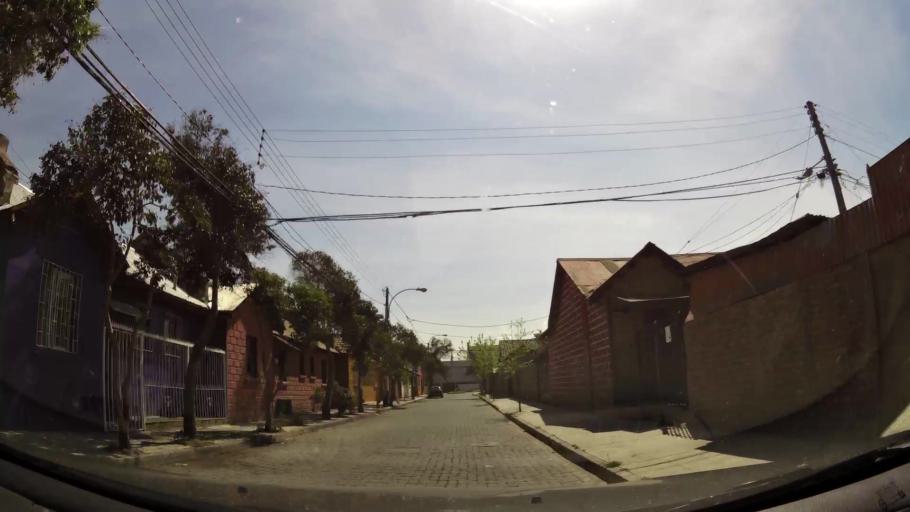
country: CL
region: Santiago Metropolitan
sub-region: Provincia de Cordillera
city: Puente Alto
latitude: -33.6128
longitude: -70.5677
